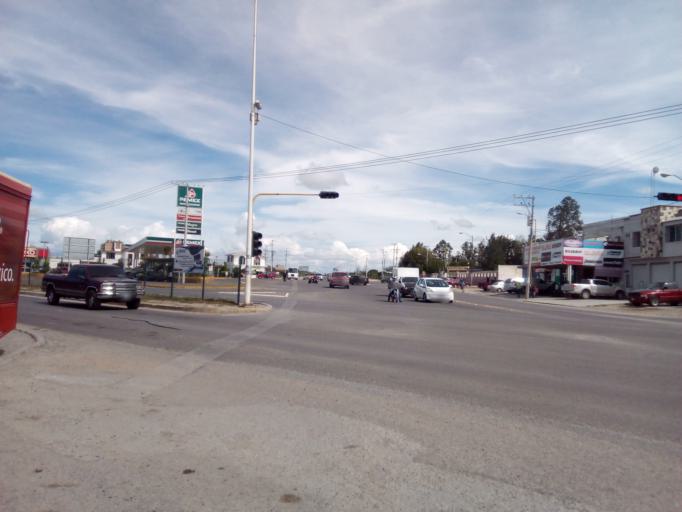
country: MX
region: Guerrero
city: San Luis de la Paz
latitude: 21.2889
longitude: -100.5104
